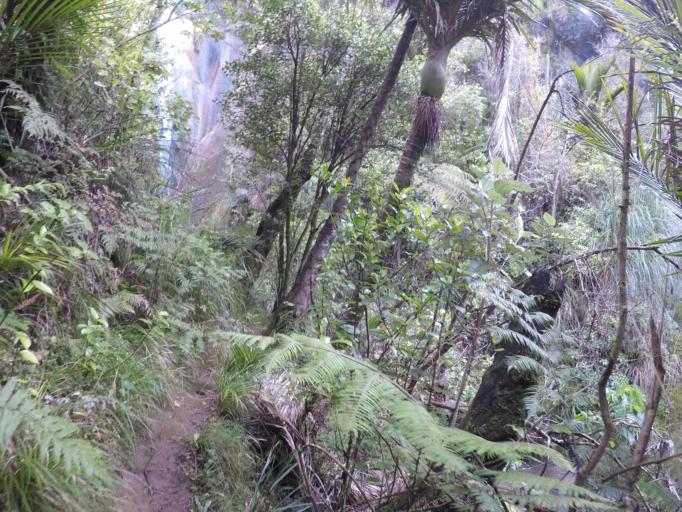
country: NZ
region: Bay of Plenty
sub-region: Western Bay of Plenty District
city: Waihi Beach
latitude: -37.3806
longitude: 175.9249
